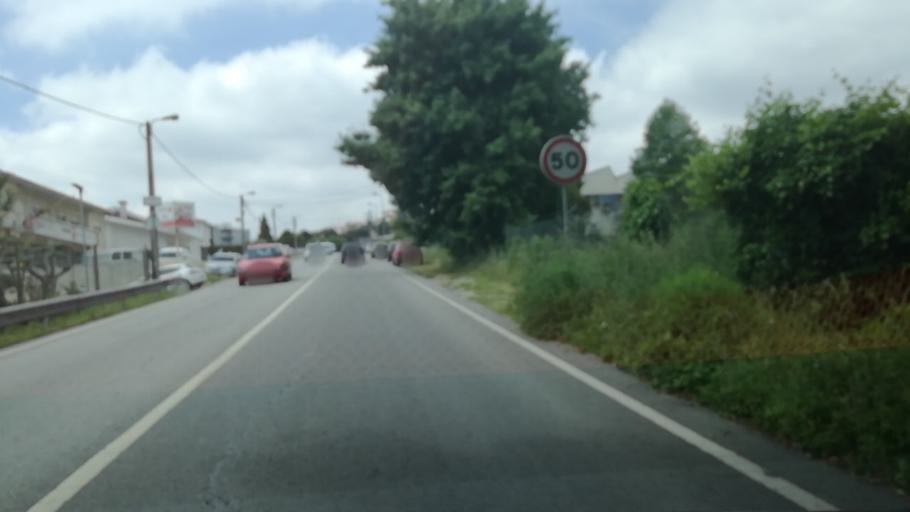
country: PT
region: Braga
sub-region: Vila Nova de Famalicao
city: Calendario
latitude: 41.3925
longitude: -8.5242
